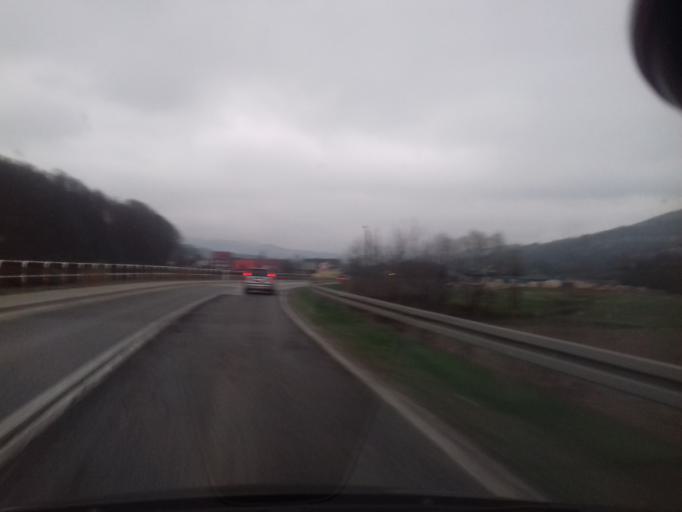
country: PL
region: Lesser Poland Voivodeship
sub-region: Powiat myslenicki
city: Lubien
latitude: 49.7038
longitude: 20.0318
